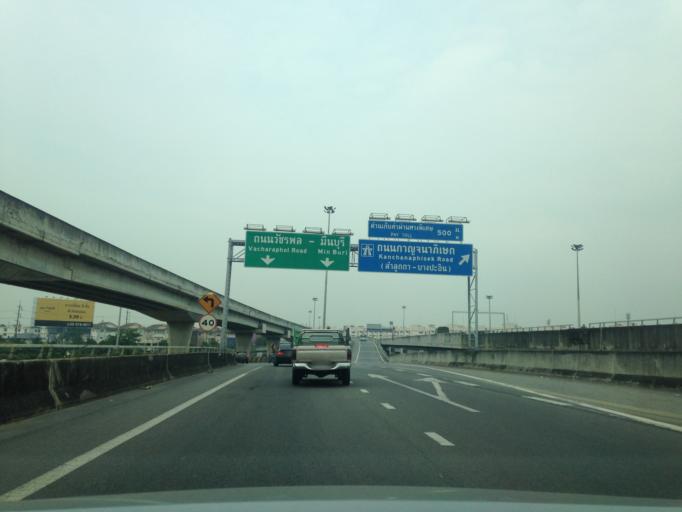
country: TH
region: Bangkok
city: Bang Khen
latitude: 13.8510
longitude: 100.6399
